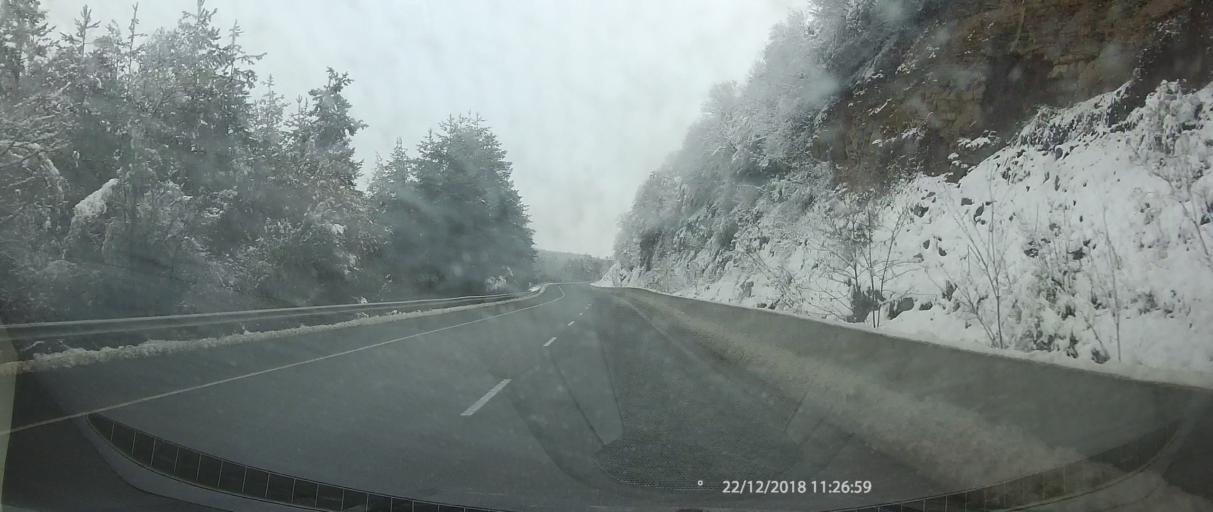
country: BG
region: Kyustendil
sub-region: Obshtina Bobovdol
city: Bobovdol
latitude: 42.2721
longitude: 22.9269
